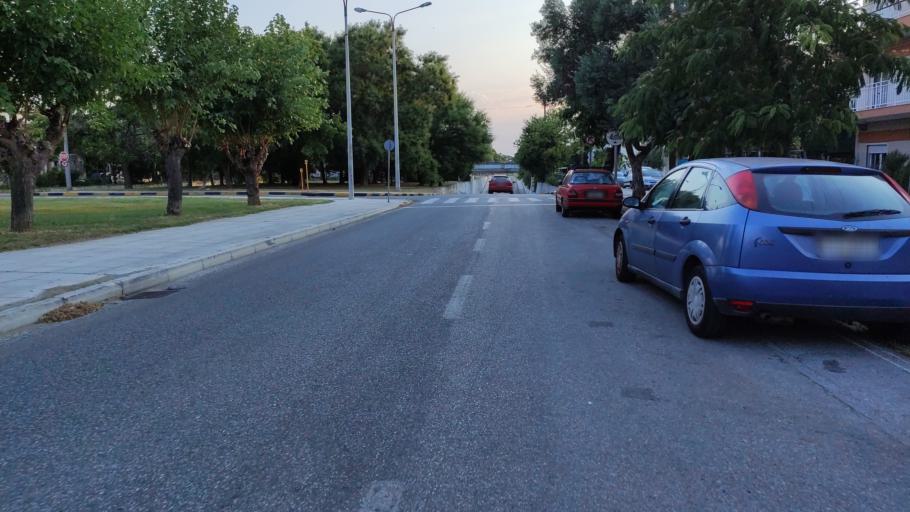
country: GR
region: East Macedonia and Thrace
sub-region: Nomos Rodopis
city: Komotini
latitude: 41.1153
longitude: 25.3922
